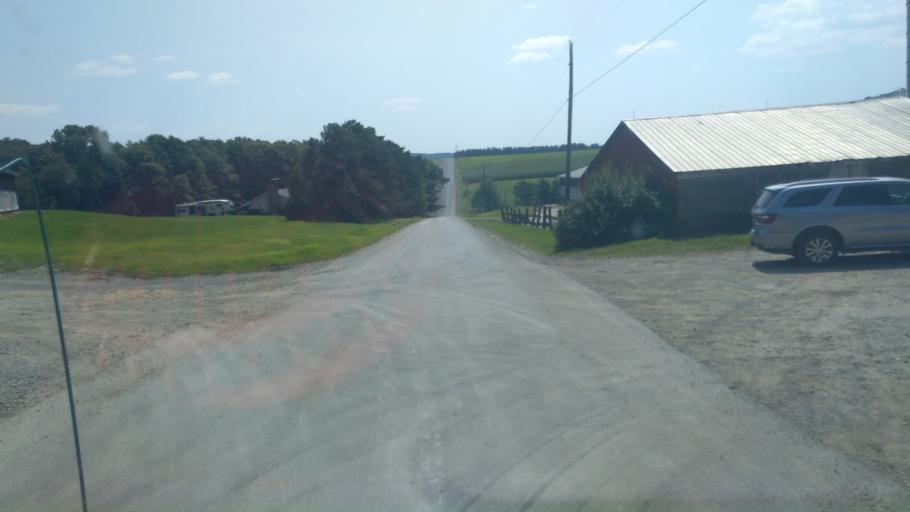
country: US
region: New York
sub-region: Steuben County
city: Canisteo
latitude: 42.3431
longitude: -77.5775
